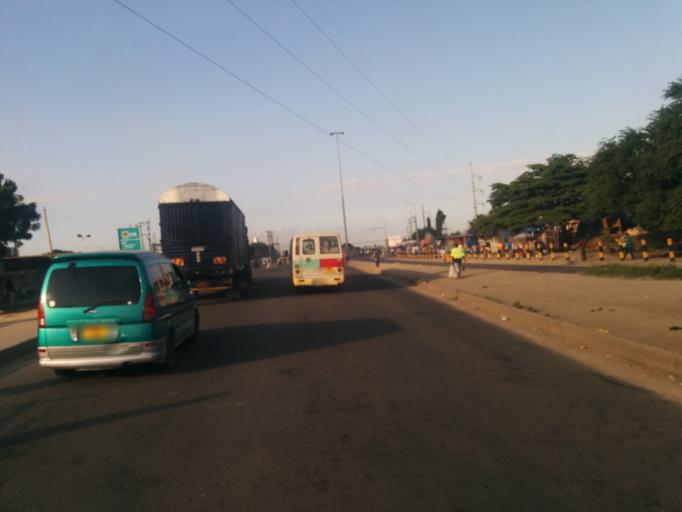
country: TZ
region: Dar es Salaam
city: Magomeni
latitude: -6.7913
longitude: 39.2086
